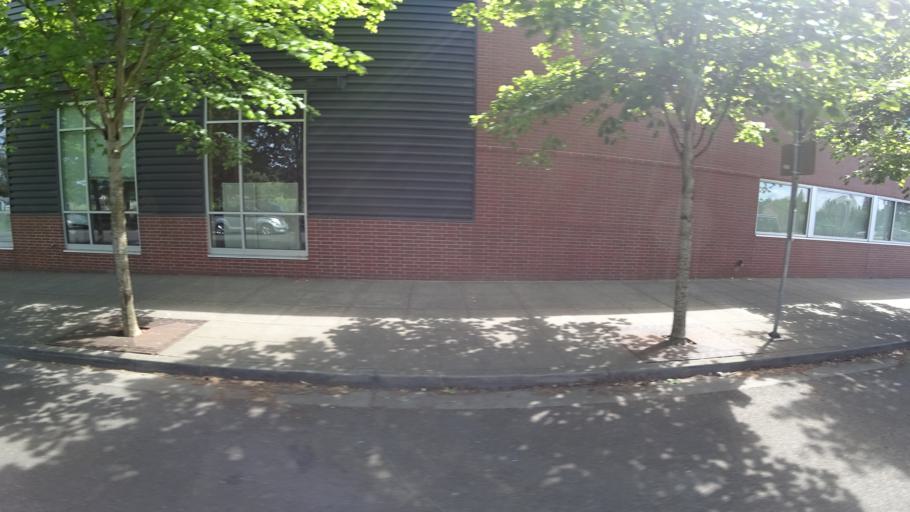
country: US
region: Washington
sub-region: Clark County
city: Vancouver
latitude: 45.5886
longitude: -122.7130
